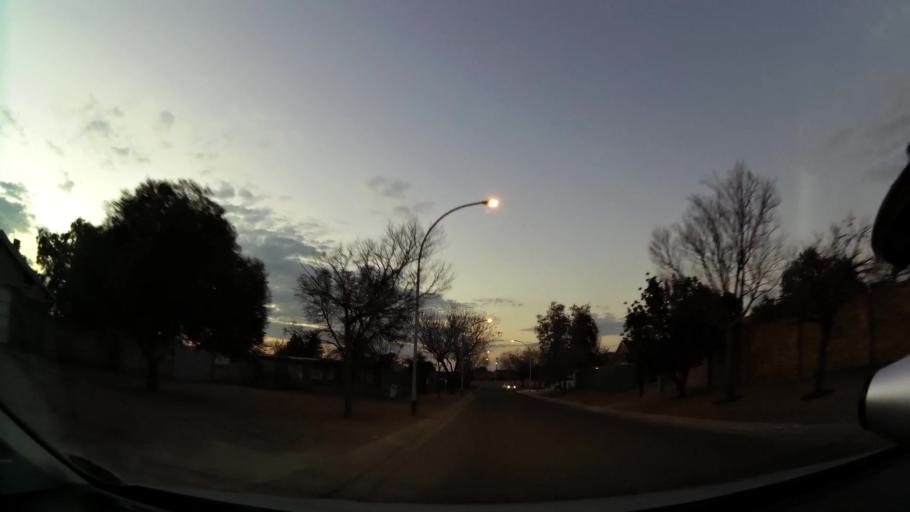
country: ZA
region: Orange Free State
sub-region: Mangaung Metropolitan Municipality
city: Bloemfontein
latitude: -29.1547
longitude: 26.1934
